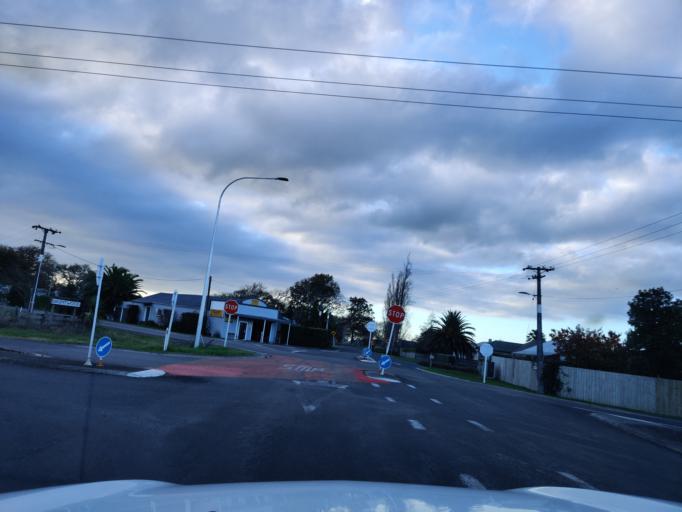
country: NZ
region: Waikato
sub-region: Waipa District
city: Cambridge
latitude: -37.8456
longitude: 175.4390
